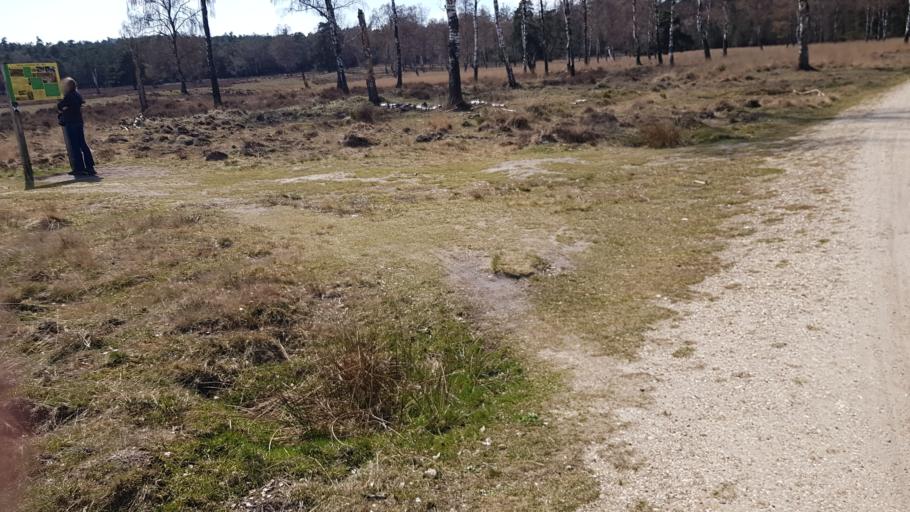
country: NL
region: Gelderland
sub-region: Gemeente Apeldoorn
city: Loenen
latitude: 52.0799
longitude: 5.9995
